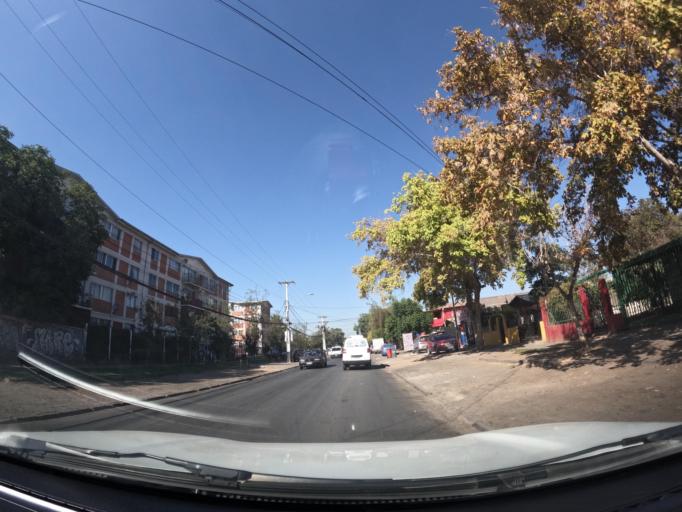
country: CL
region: Santiago Metropolitan
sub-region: Provincia de Santiago
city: Villa Presidente Frei, Nunoa, Santiago, Chile
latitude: -33.4700
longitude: -70.5622
